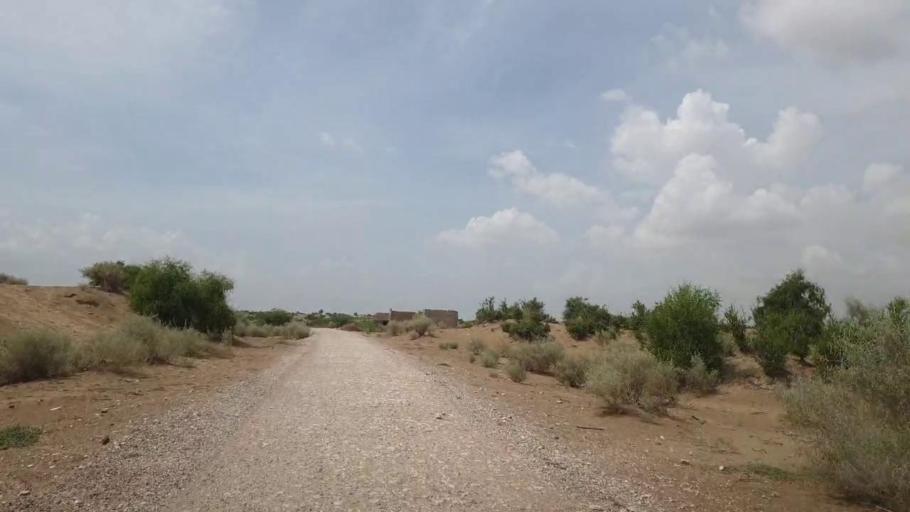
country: PK
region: Sindh
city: Kot Diji
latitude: 27.2500
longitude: 69.0774
